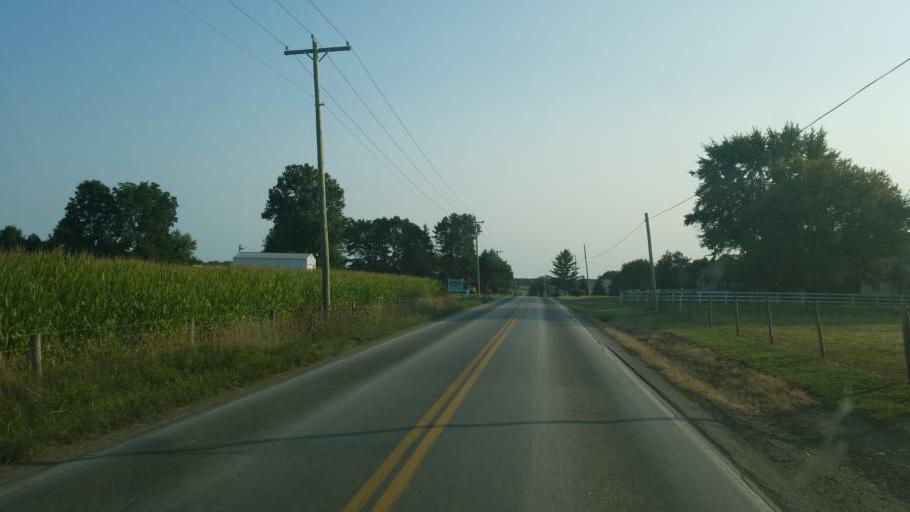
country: US
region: Ohio
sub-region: Wayne County
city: Apple Creek
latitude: 40.7677
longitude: -81.7926
